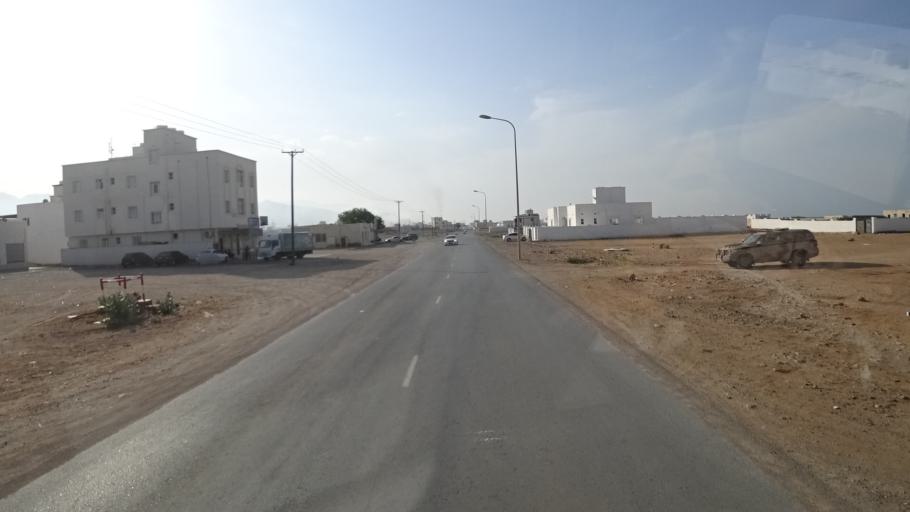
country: OM
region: Ash Sharqiyah
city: Sur
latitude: 22.6141
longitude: 59.4631
